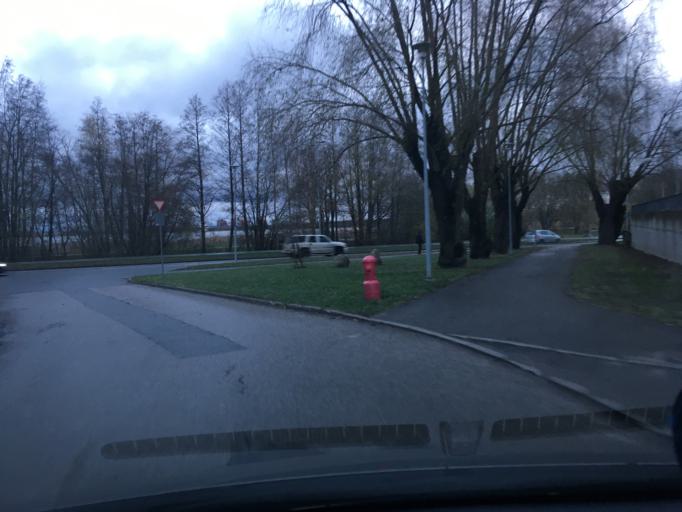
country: EE
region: Harju
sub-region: Saue vald
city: Laagri
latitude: 59.4287
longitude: 24.6532
